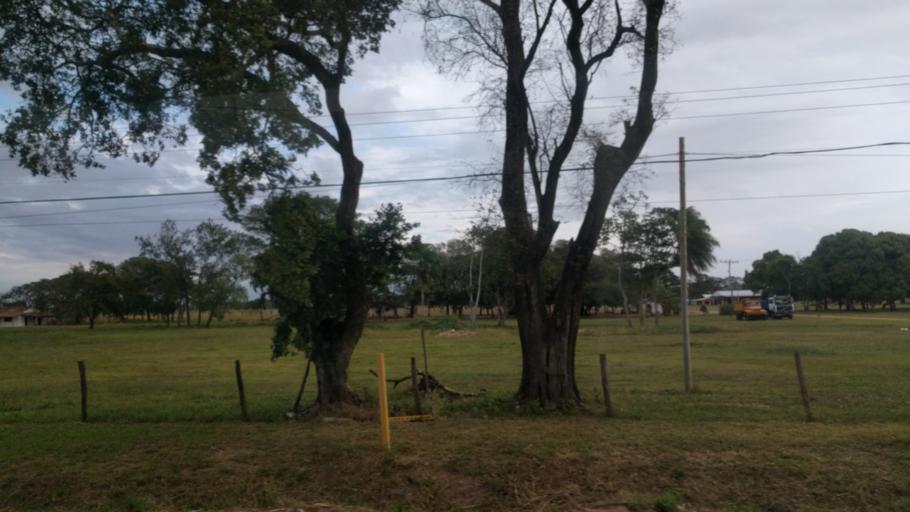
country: BO
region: Santa Cruz
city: Montero
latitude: -17.3787
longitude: -63.2282
